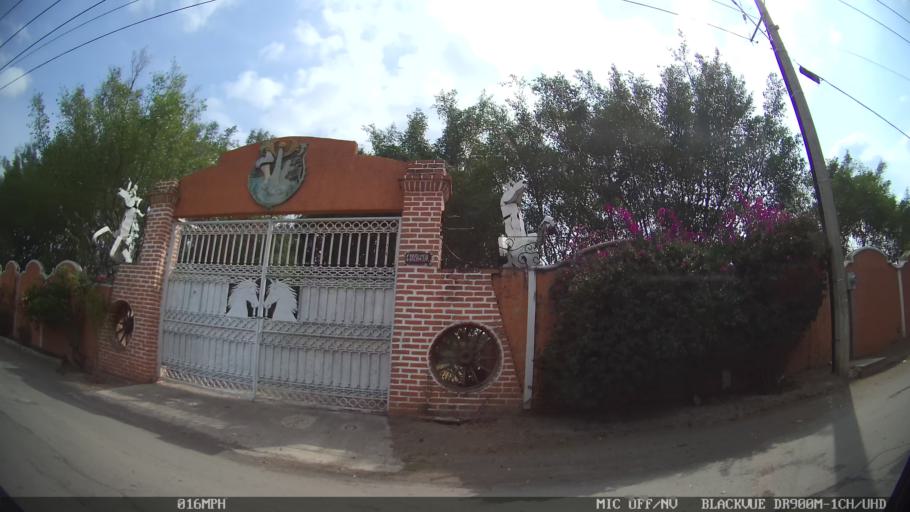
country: MX
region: Jalisco
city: Tonala
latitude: 20.6390
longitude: -103.2221
